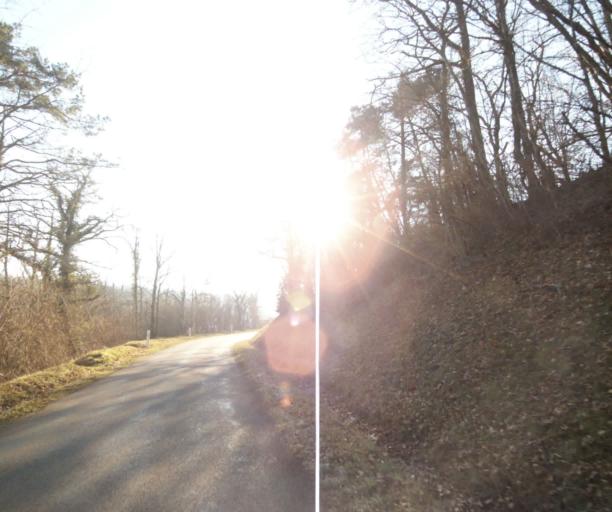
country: FR
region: Champagne-Ardenne
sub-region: Departement de la Haute-Marne
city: Chevillon
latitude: 48.5478
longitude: 5.1260
